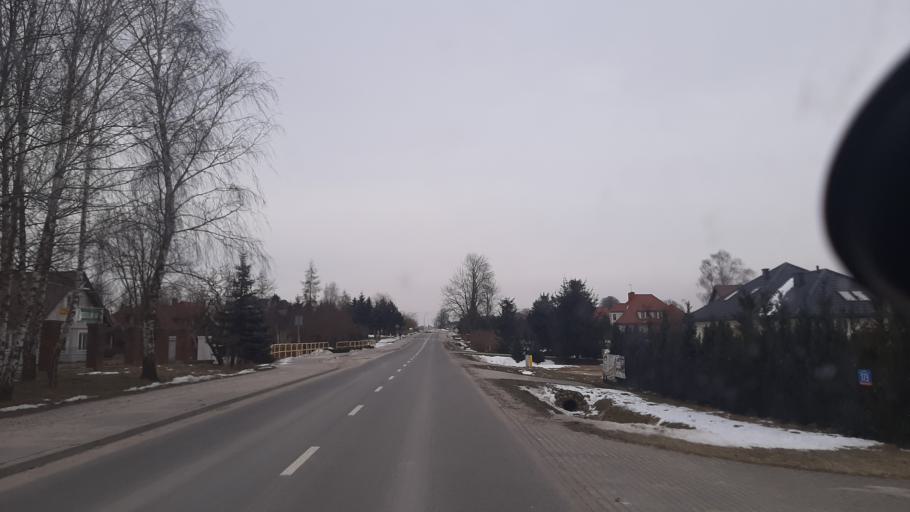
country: PL
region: Lublin Voivodeship
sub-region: Powiat lubelski
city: Lublin
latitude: 51.3036
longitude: 22.5397
